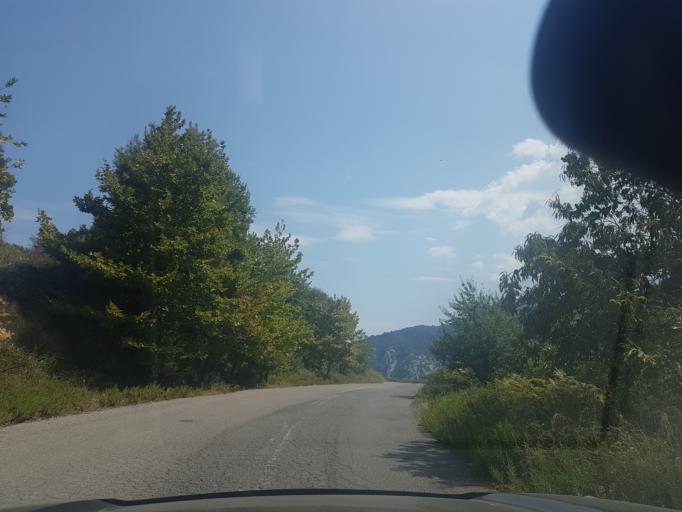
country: GR
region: Central Greece
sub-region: Nomos Evvoias
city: Yimnon
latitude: 38.6249
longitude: 23.8925
